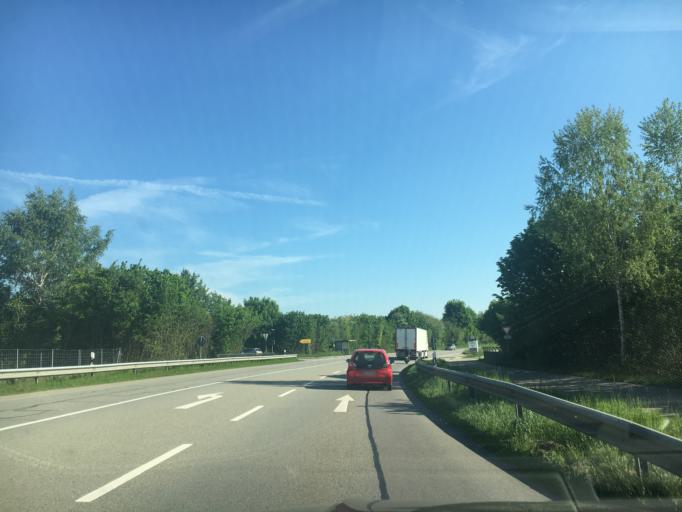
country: DE
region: Bavaria
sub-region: Upper Bavaria
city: Unterneukirchen
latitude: 48.1779
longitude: 12.6307
